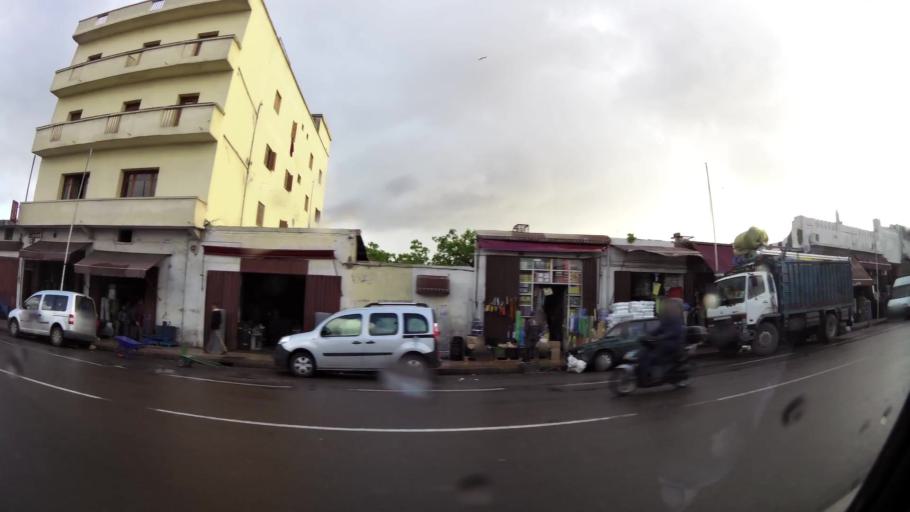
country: MA
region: Grand Casablanca
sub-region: Casablanca
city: Casablanca
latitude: 33.5826
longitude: -7.6032
